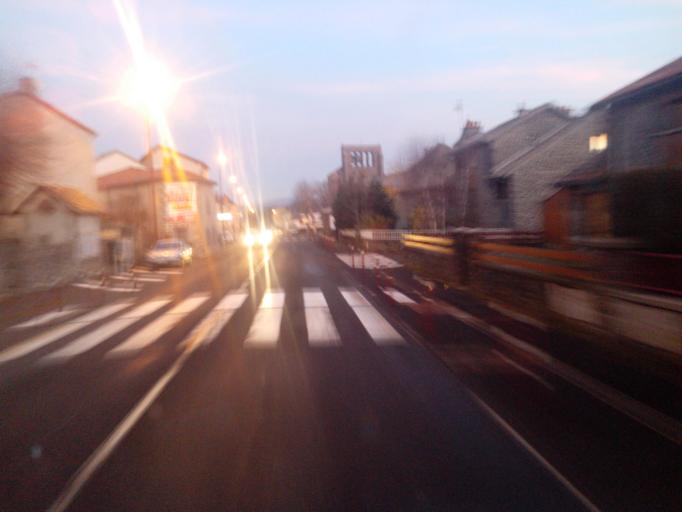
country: FR
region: Auvergne
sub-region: Departement du Cantal
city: Saint-Flour
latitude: 45.0523
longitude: 3.0379
